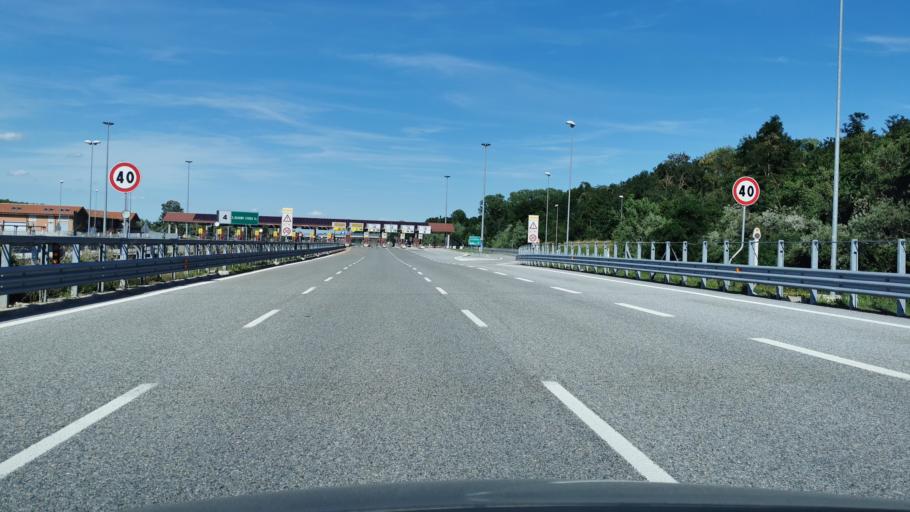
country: IT
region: Piedmont
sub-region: Provincia di Cuneo
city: Castelletto Stura
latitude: 44.4298
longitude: 7.6063
